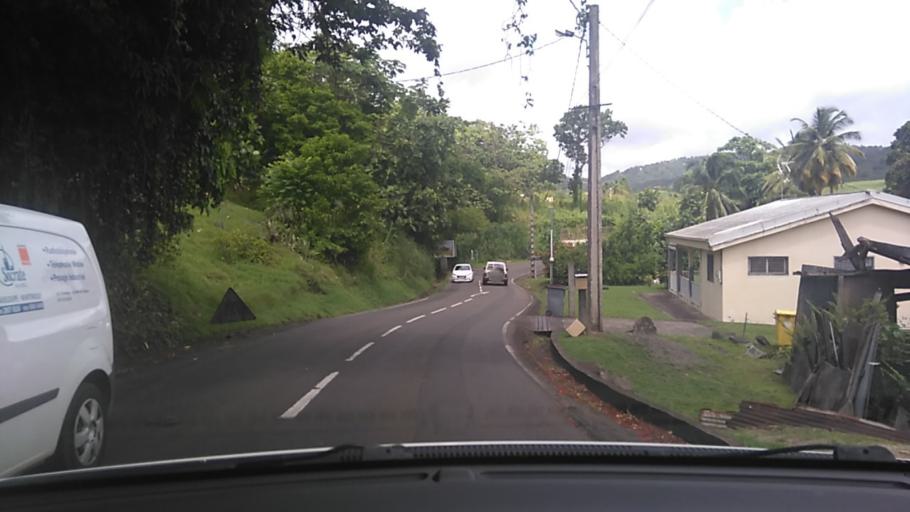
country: MQ
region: Martinique
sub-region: Martinique
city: Saint-Esprit
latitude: 14.5599
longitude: -60.9321
